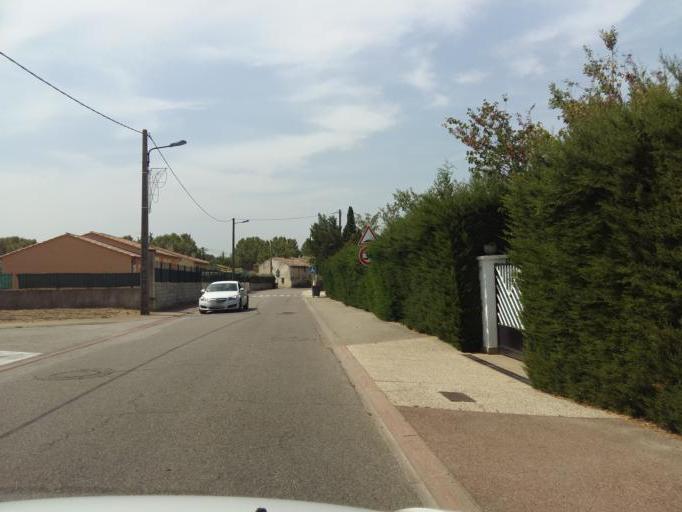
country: FR
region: Provence-Alpes-Cote d'Azur
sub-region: Departement du Vaucluse
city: Lapalud
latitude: 44.3087
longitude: 4.6878
